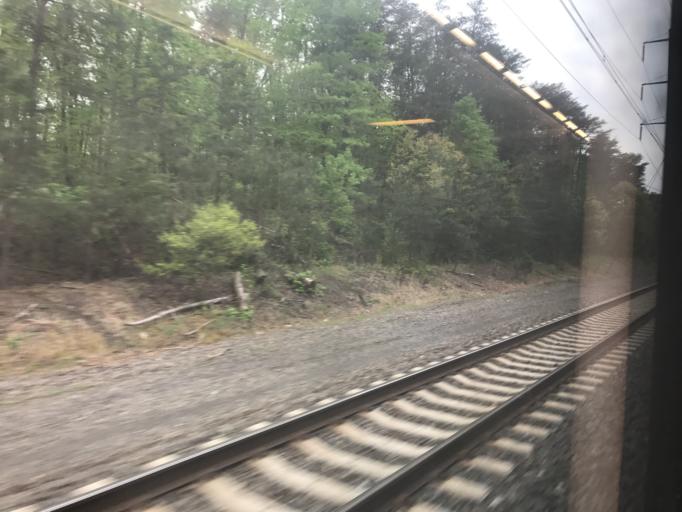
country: US
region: Maryland
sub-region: Prince George's County
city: Glenn Dale
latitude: 39.0015
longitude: -76.7900
